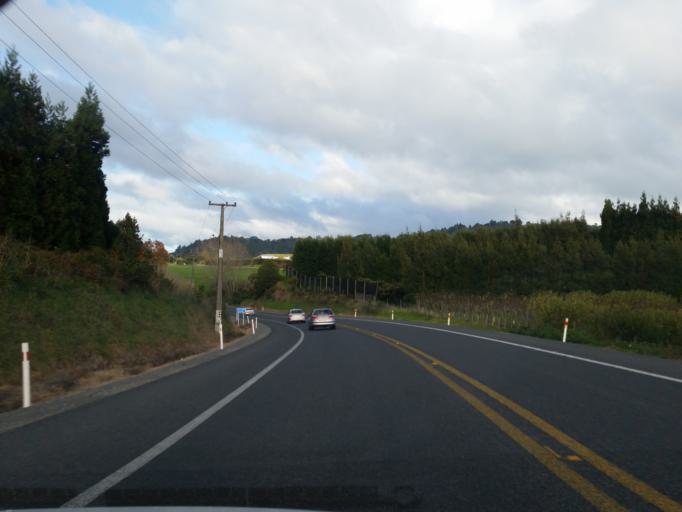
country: NZ
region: Bay of Plenty
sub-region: Tauranga City
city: Tauranga
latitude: -37.6899
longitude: 176.0414
